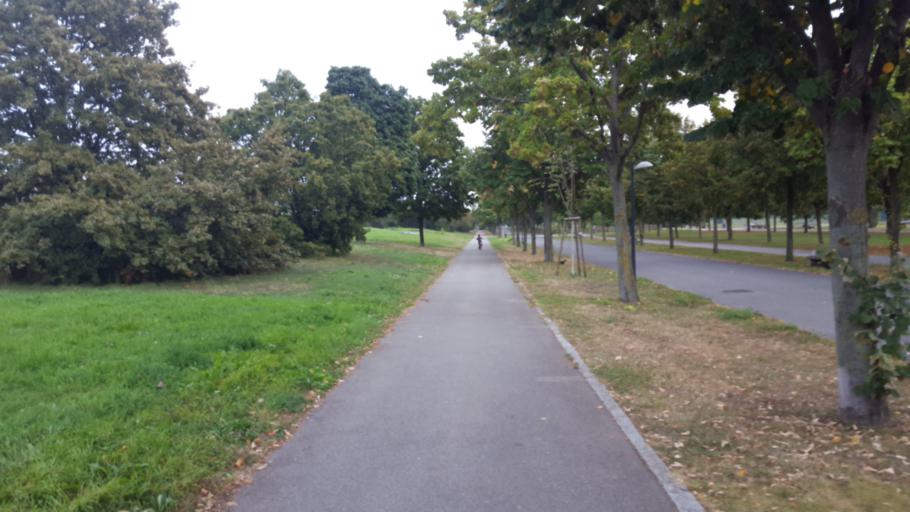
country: AT
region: Vienna
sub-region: Wien Stadt
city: Vienna
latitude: 48.2227
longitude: 16.4232
